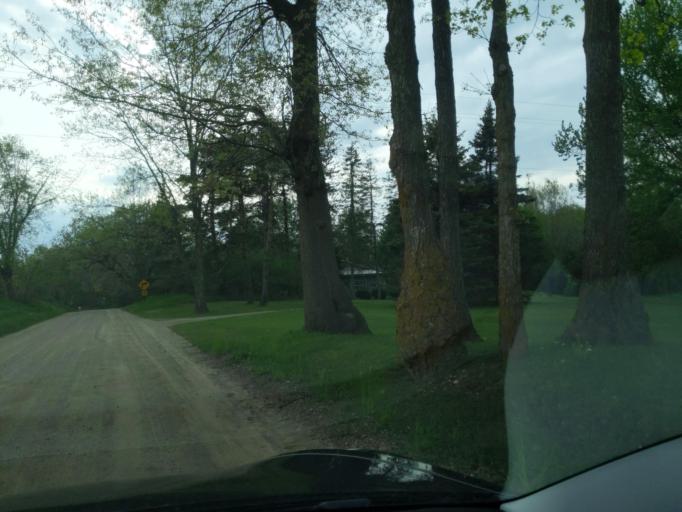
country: US
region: Michigan
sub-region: Ingham County
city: Stockbridge
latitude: 42.4246
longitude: -84.1364
